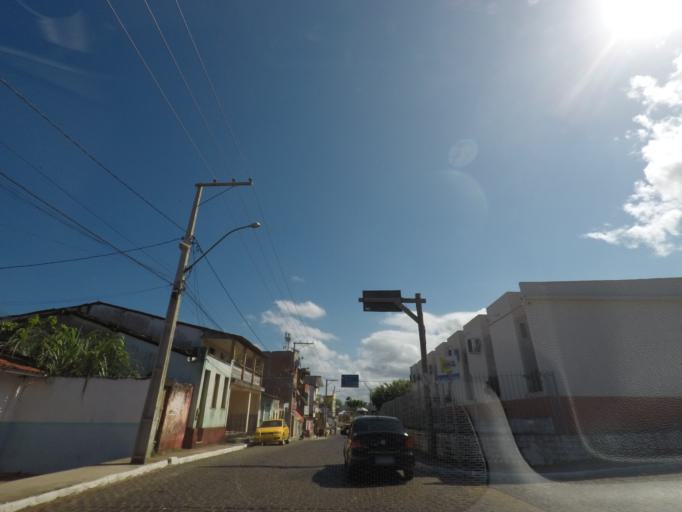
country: BR
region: Bahia
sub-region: Camamu
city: Camamu
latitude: -13.9427
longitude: -39.1037
